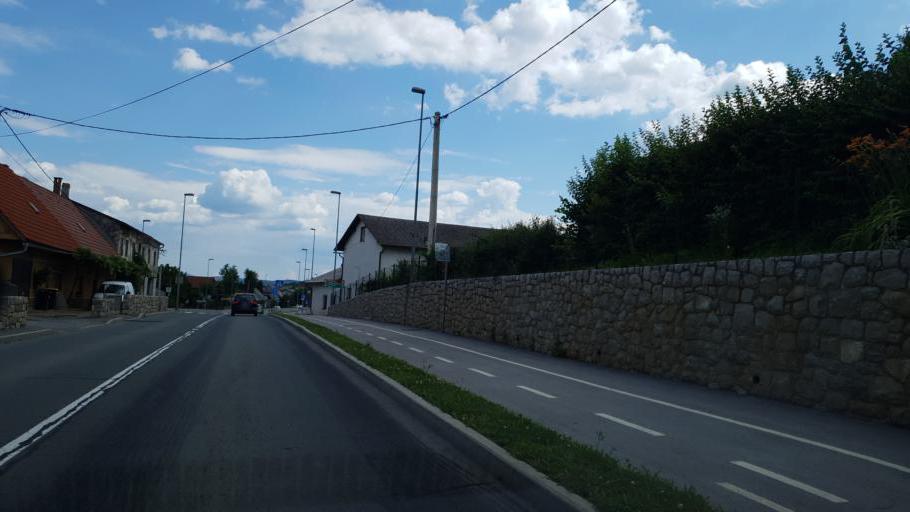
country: SI
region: Pivka
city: Pivka
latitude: 45.6913
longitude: 14.1953
